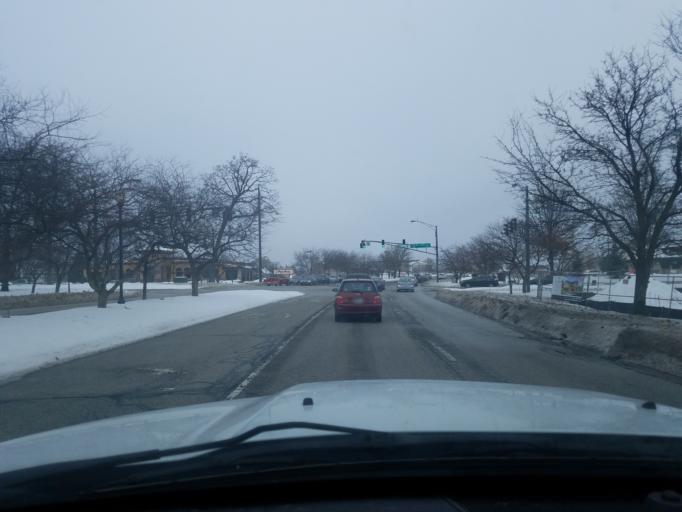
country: US
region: Indiana
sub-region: Saint Joseph County
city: Mishawaka
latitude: 41.7039
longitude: -86.1826
